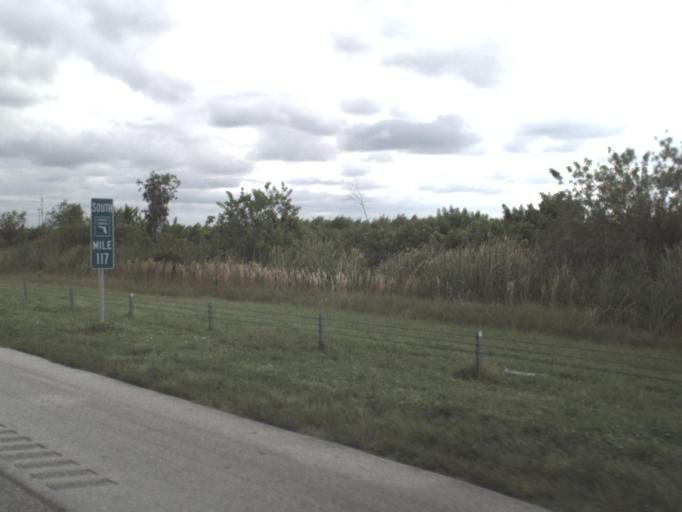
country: US
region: Florida
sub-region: Palm Beach County
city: Limestone Creek
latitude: 26.9479
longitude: -80.1610
